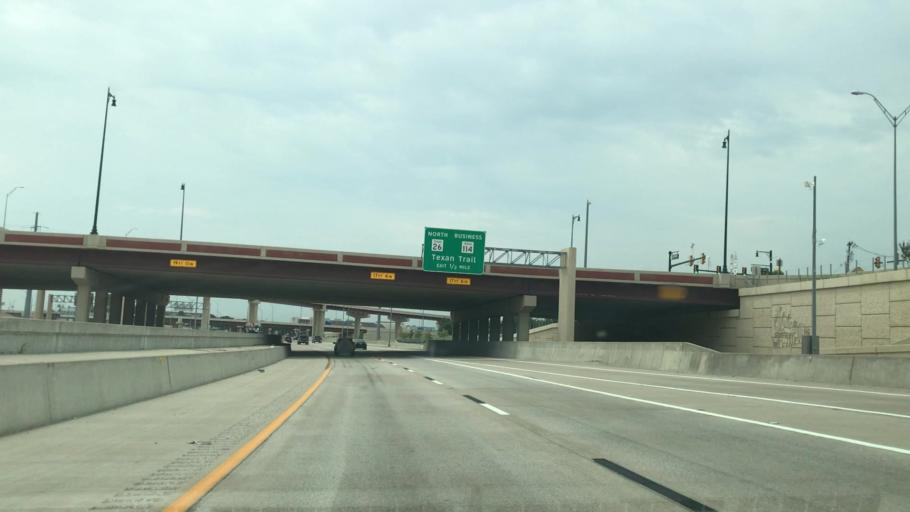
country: US
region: Texas
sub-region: Tarrant County
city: Grapevine
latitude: 32.9255
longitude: -97.0895
